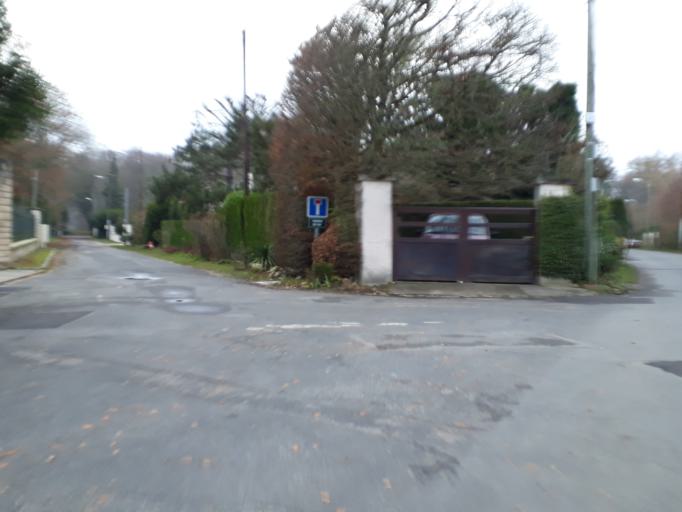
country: FR
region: Ile-de-France
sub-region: Departement de Seine-et-Marne
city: Bois-le-Roi
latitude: 48.4744
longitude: 2.6858
